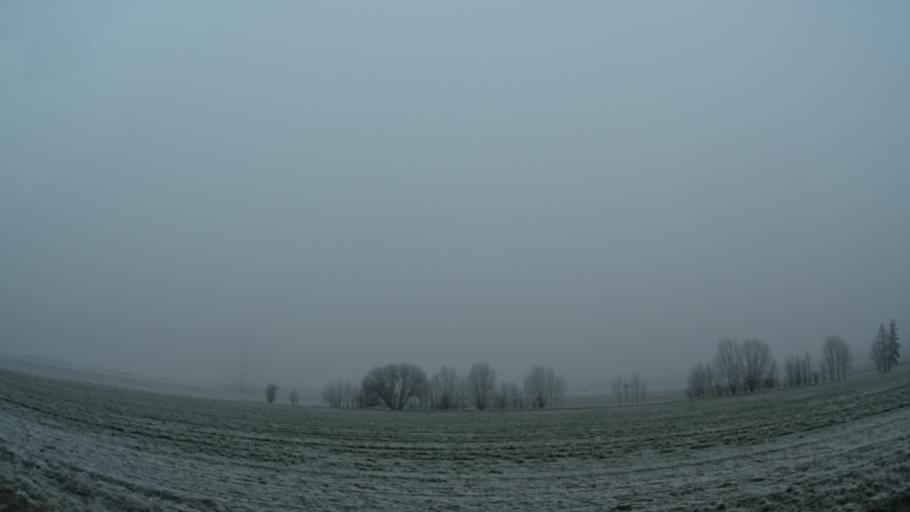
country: DE
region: Bavaria
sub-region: Regierungsbezirk Unterfranken
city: Lulsfeld
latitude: 49.8655
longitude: 10.3133
